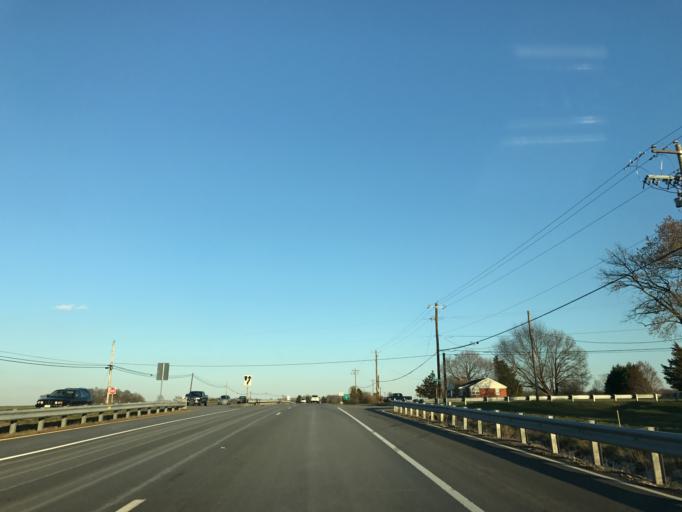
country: US
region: Maryland
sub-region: Queen Anne's County
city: Centreville
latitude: 38.9646
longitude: -76.1071
